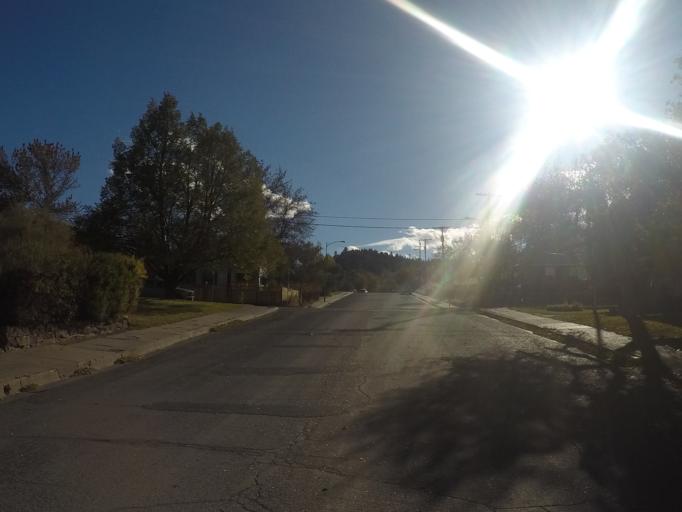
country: US
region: Montana
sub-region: Lewis and Clark County
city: Helena
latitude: 46.5821
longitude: -112.0378
